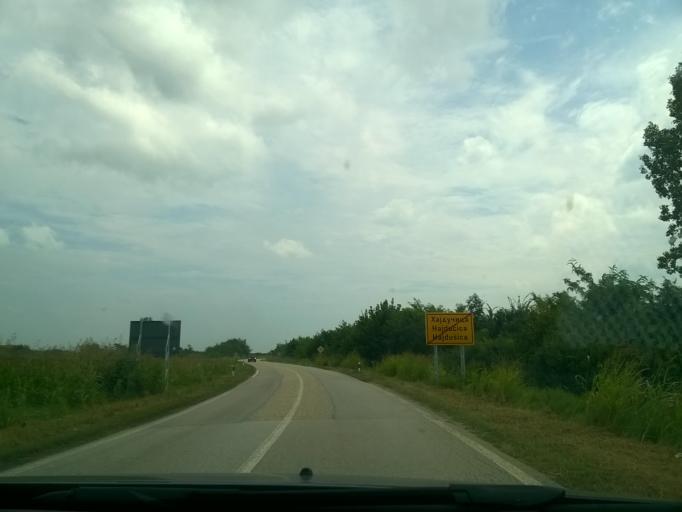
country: RS
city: Hajducica
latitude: 45.2516
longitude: 20.9721
